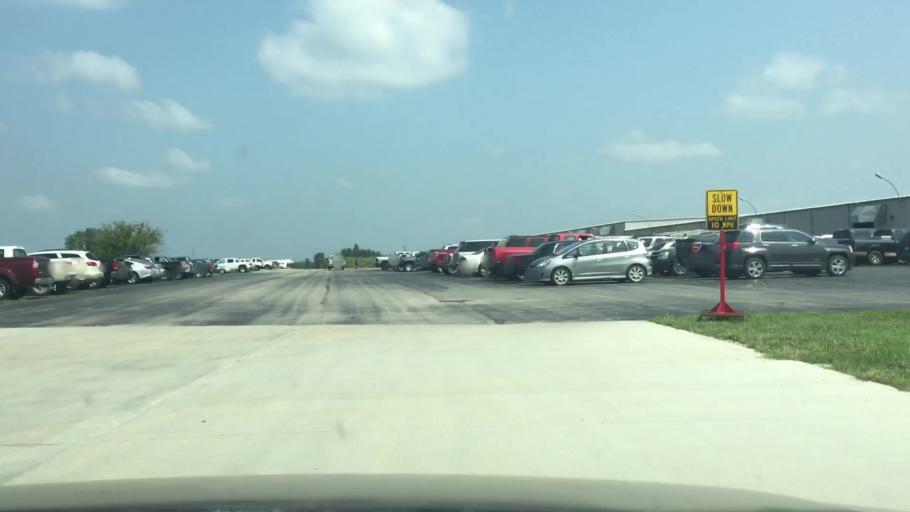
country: US
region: Kansas
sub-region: Allen County
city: Humboldt
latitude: 37.8213
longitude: -95.4317
